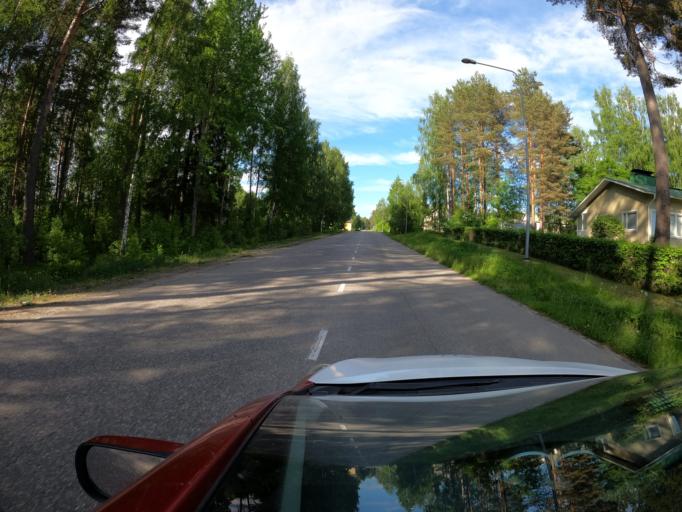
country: FI
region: Southern Savonia
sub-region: Savonlinna
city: Savonlinna
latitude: 61.8472
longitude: 28.9593
